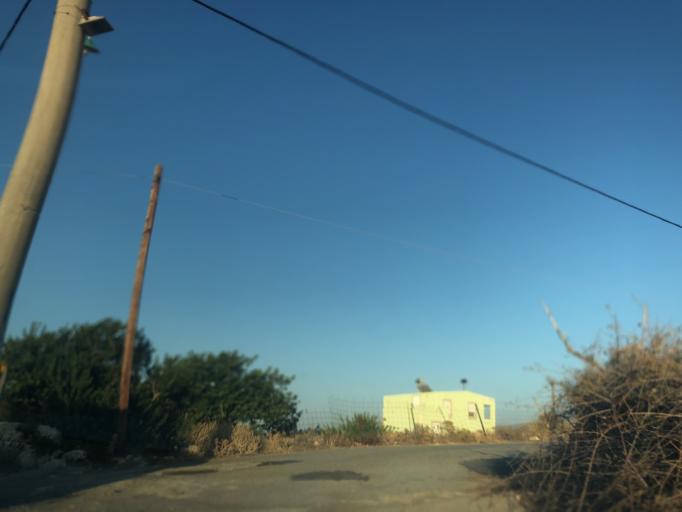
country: GR
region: Crete
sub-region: Nomos Rethymnis
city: Atsipopoulon
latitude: 35.3582
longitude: 24.3967
